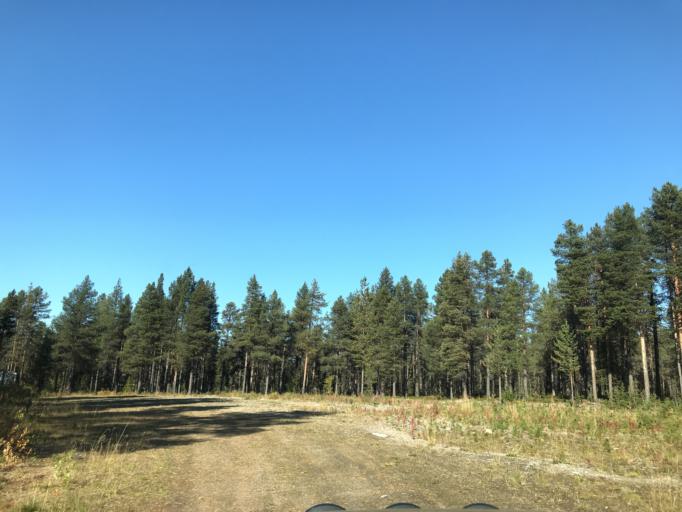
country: SE
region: Norrbotten
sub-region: Gallivare Kommun
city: Malmberget
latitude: 67.6495
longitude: 21.0822
